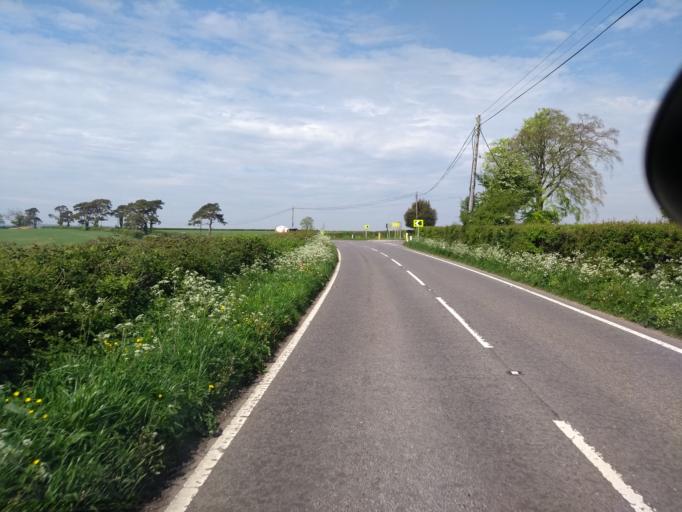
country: GB
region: England
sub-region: Somerset
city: Chard
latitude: 50.8846
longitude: -3.0091
